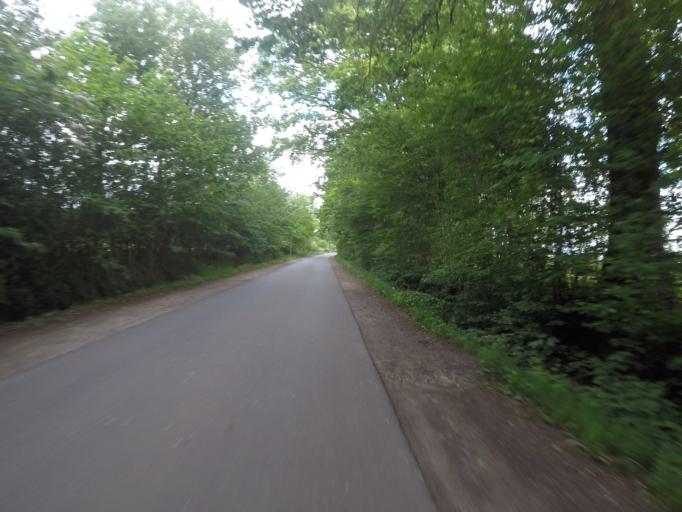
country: DE
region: Schleswig-Holstein
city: Quickborn
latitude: 53.7026
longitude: 9.9205
